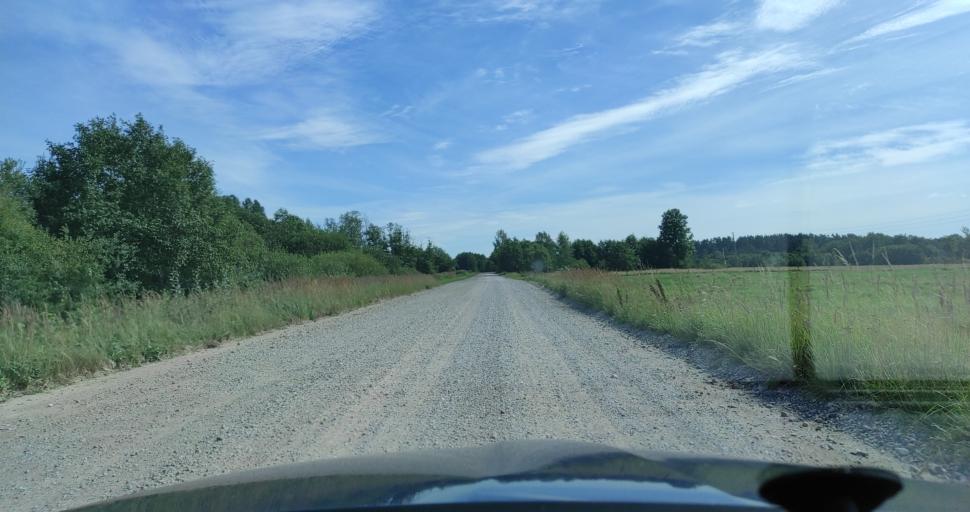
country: LV
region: Durbe
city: Liegi
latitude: 56.7485
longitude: 21.3657
